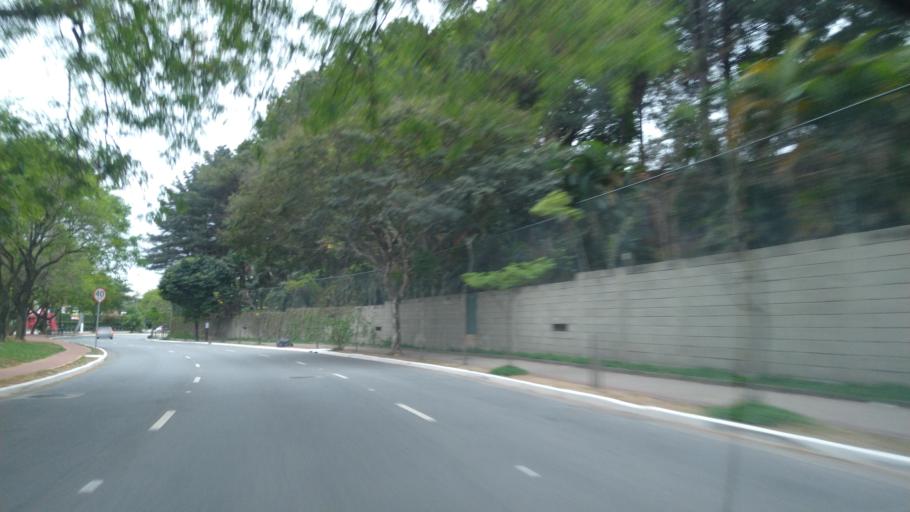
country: BR
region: Sao Paulo
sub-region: Taboao Da Serra
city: Taboao da Serra
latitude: -23.5943
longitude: -46.7205
